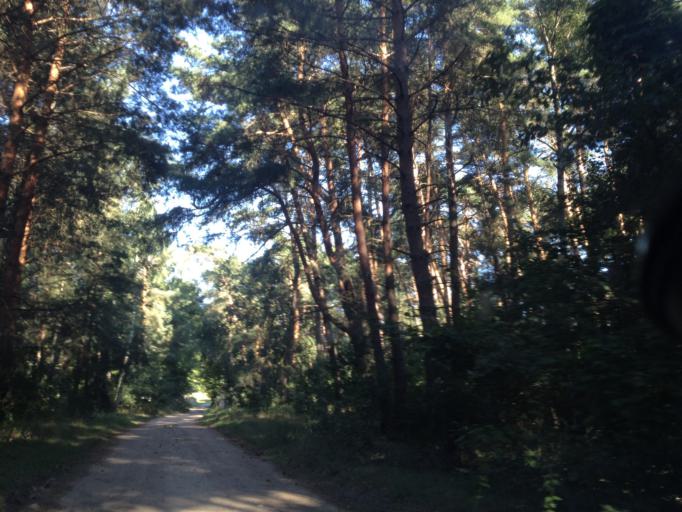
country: PL
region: Greater Poland Voivodeship
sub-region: Powiat sredzki
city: Zaniemysl
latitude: 52.1028
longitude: 17.1335
